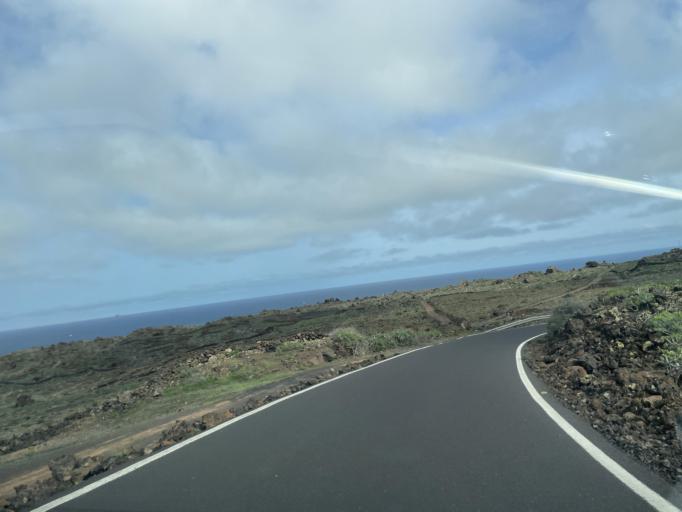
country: ES
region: Canary Islands
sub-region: Provincia de Las Palmas
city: Haria
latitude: 29.1977
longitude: -13.4532
